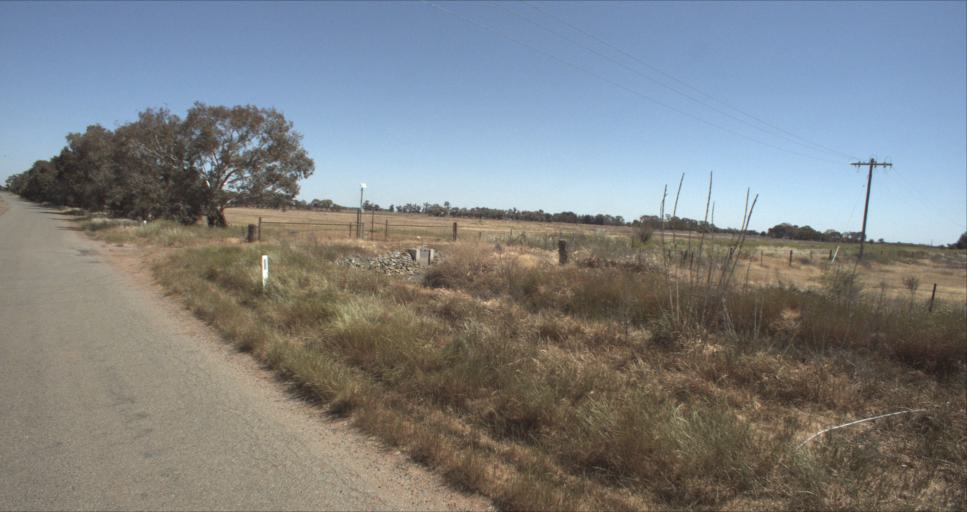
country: AU
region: New South Wales
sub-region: Leeton
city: Leeton
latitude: -34.4962
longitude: 146.4212
